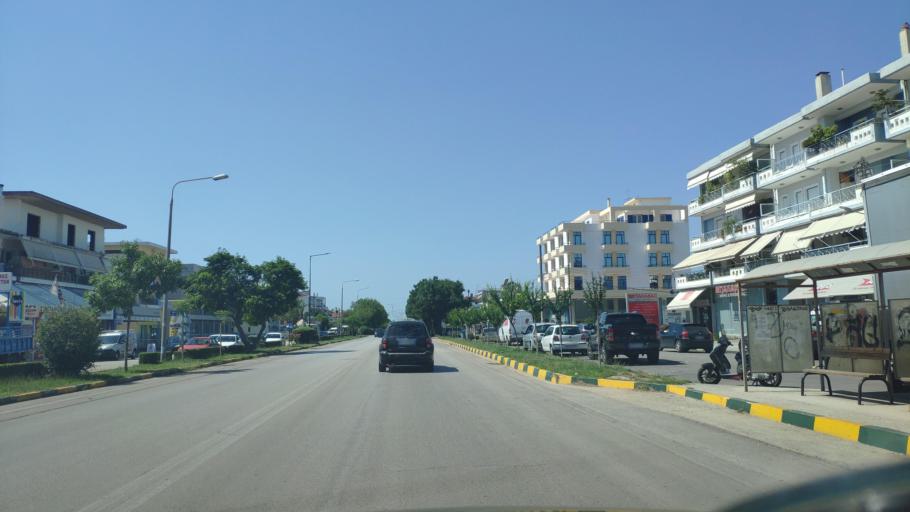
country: GR
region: Epirus
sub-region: Nomos Artas
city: Arta
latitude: 39.1600
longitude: 20.9803
